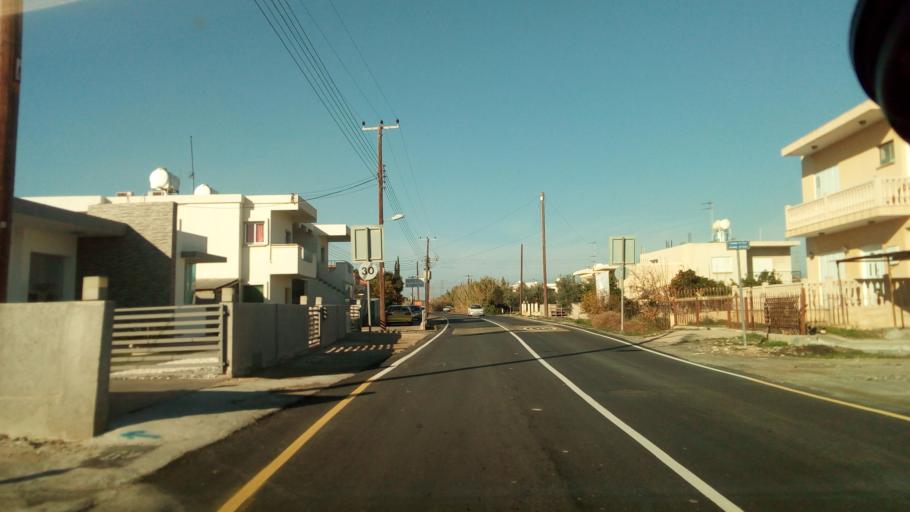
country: CY
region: Larnaka
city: Xylotymbou
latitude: 34.9975
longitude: 33.7651
